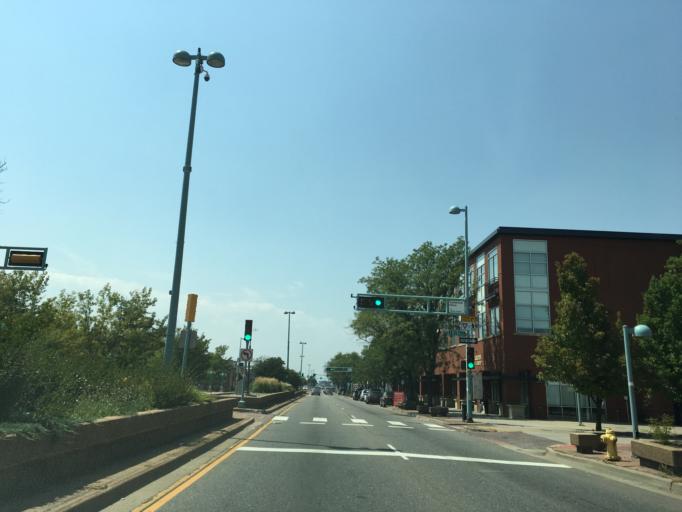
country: US
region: Colorado
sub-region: Adams County
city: Aurora
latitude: 39.7402
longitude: -104.8724
